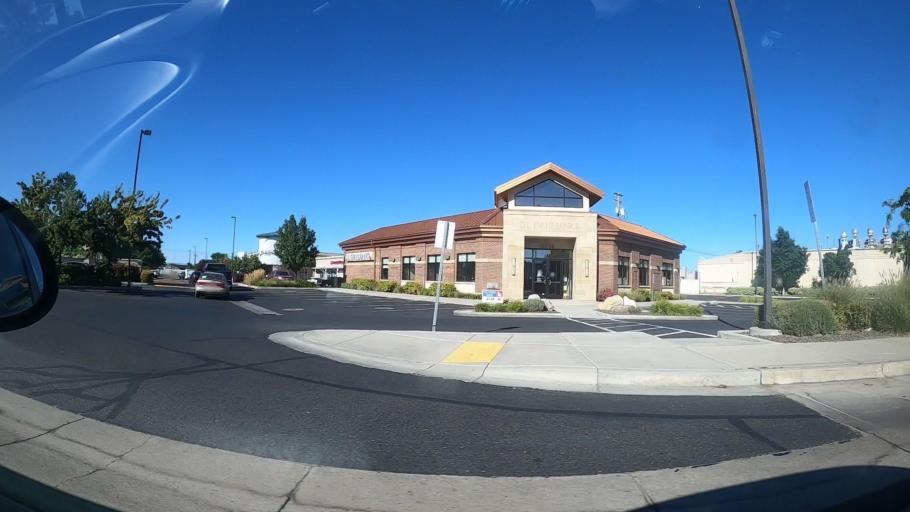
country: US
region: Idaho
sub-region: Canyon County
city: Nampa
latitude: 43.6020
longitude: -116.5979
